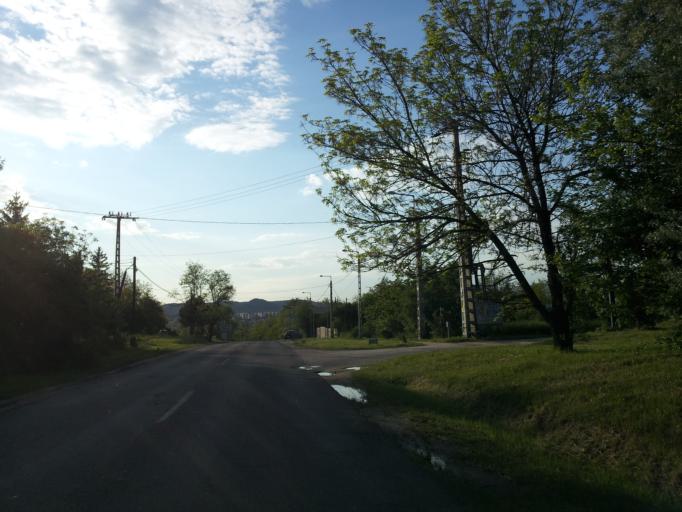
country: HU
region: Pest
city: Pilisvorosvar
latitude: 47.6012
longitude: 18.9184
